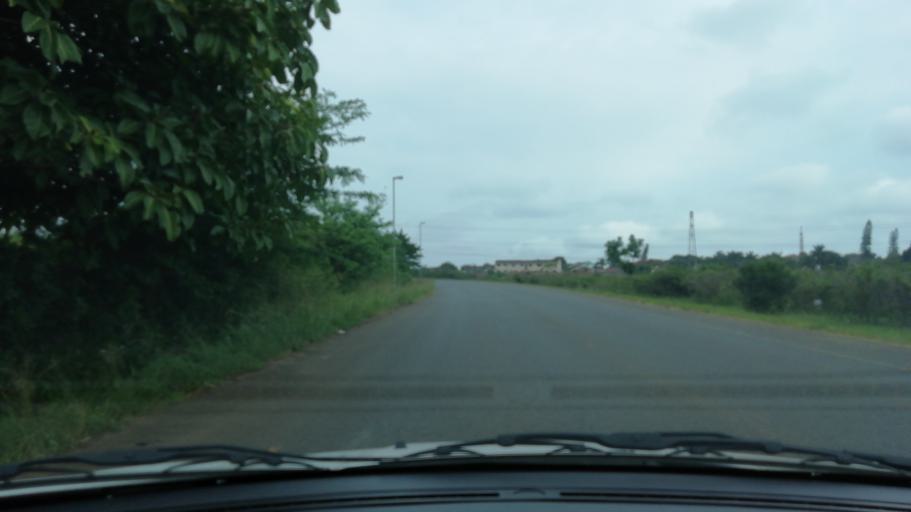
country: ZA
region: KwaZulu-Natal
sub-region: uThungulu District Municipality
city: Empangeni
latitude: -28.7345
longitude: 31.8880
